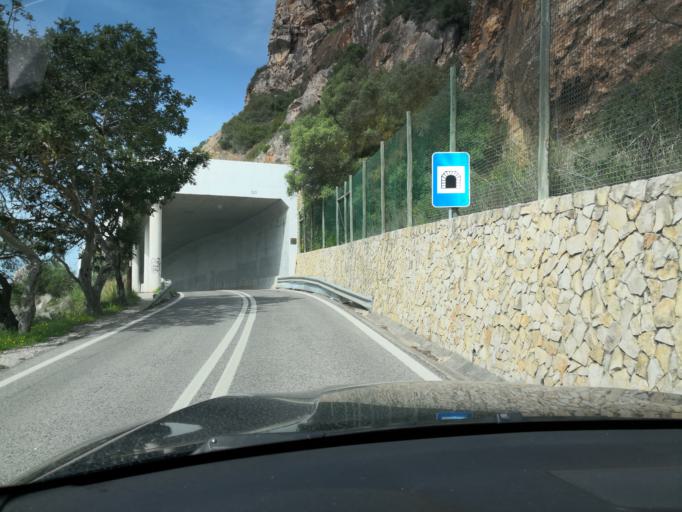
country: PT
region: Setubal
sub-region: Setubal
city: Setubal
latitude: 38.4870
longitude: -8.9387
